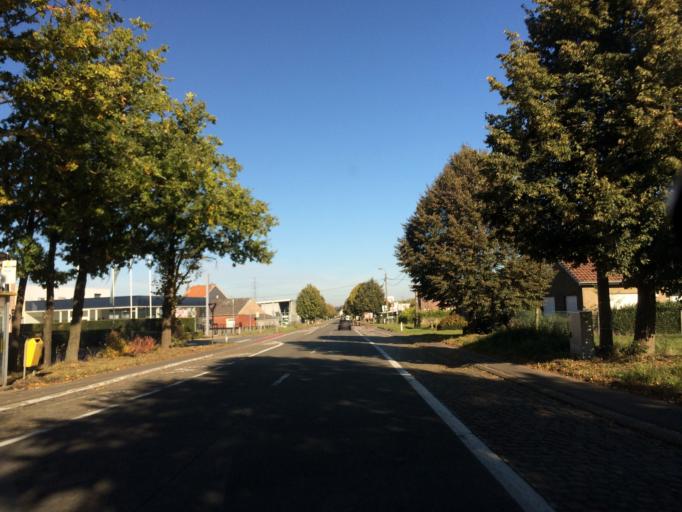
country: BE
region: Flanders
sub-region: Provincie Vlaams-Brabant
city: Merchtem
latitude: 50.9454
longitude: 4.2468
